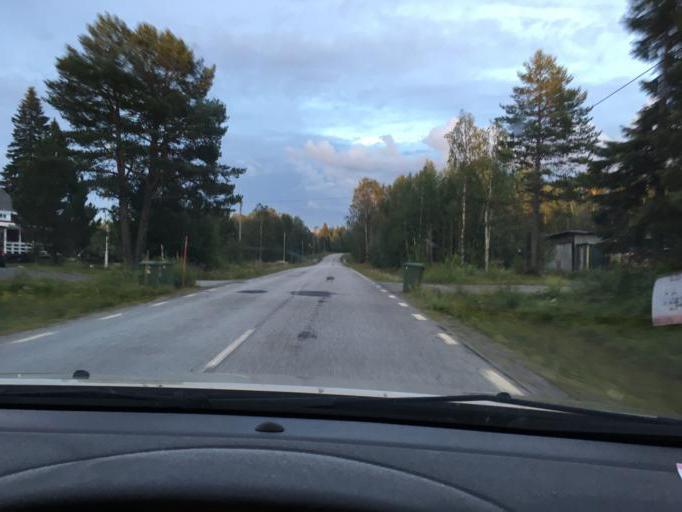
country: SE
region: Norrbotten
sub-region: Lulea Kommun
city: Ranea
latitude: 66.0468
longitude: 22.2802
